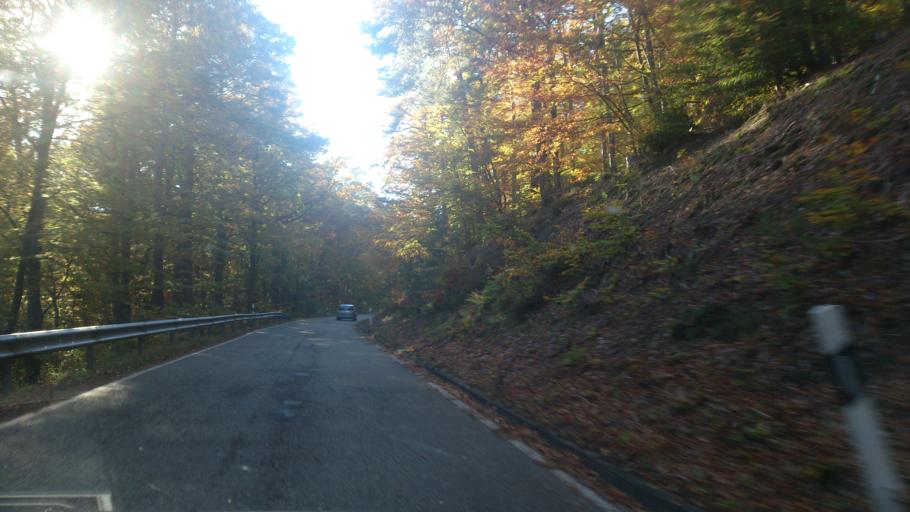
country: DE
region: Rheinland-Pfalz
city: Elmstein
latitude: 49.3356
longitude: 7.9136
